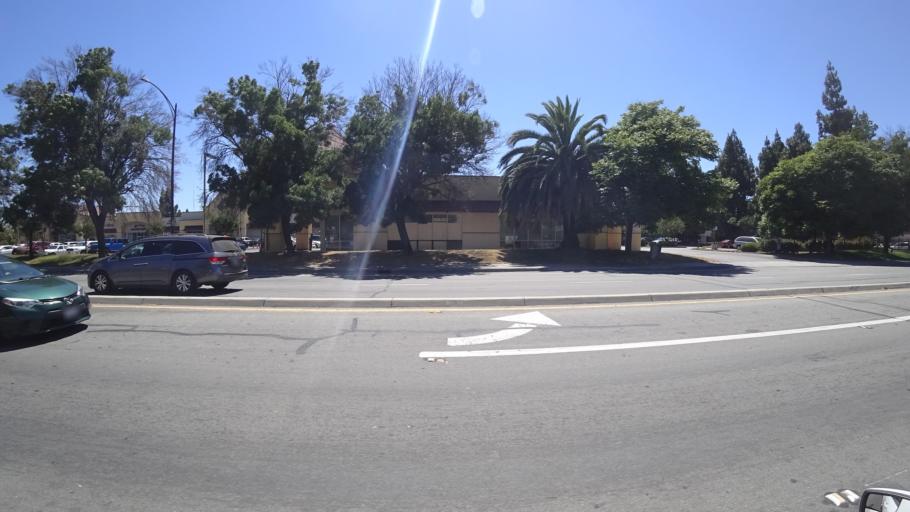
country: US
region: California
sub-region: Santa Clara County
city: San Jose
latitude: 37.3347
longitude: -121.8555
